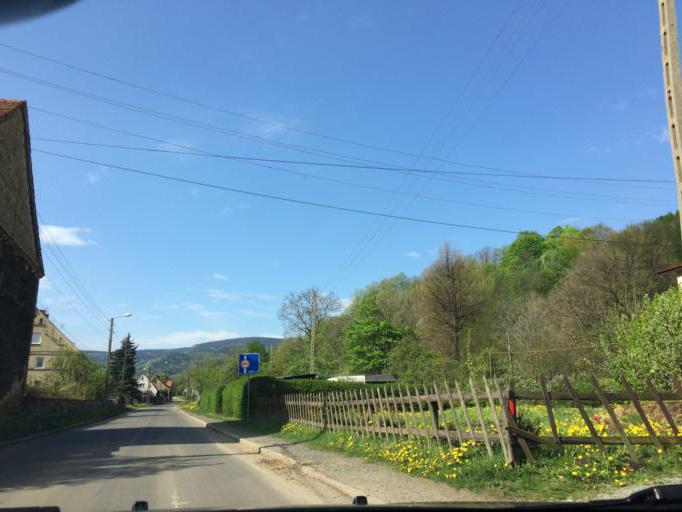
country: PL
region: Lower Silesian Voivodeship
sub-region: Powiat dzierzoniowski
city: Pieszyce
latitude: 50.6939
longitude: 16.5581
